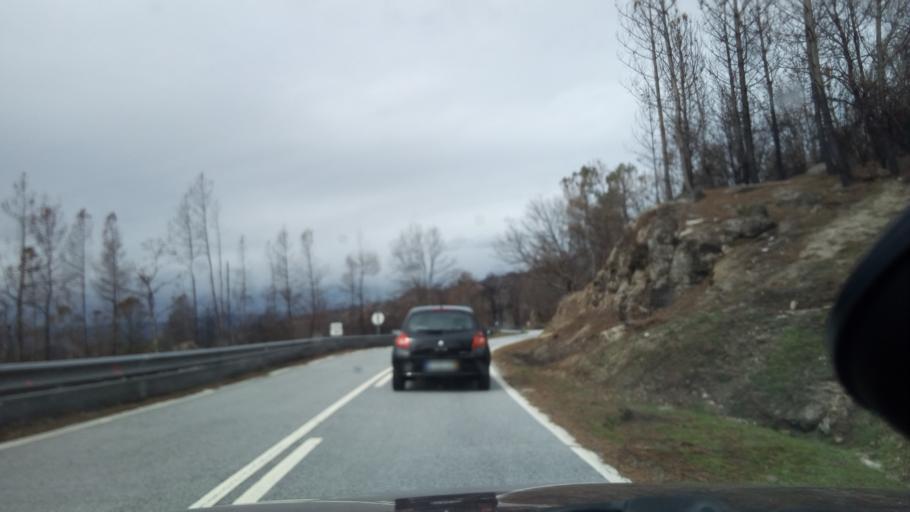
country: PT
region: Guarda
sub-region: Manteigas
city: Manteigas
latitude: 40.4655
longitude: -7.5910
